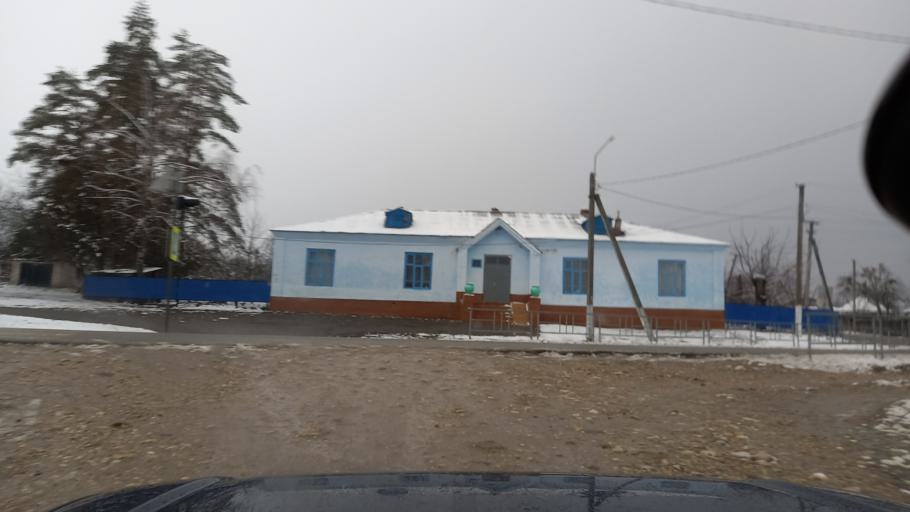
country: RU
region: Adygeya
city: Abadzekhskaya
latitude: 44.3545
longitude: 40.4098
